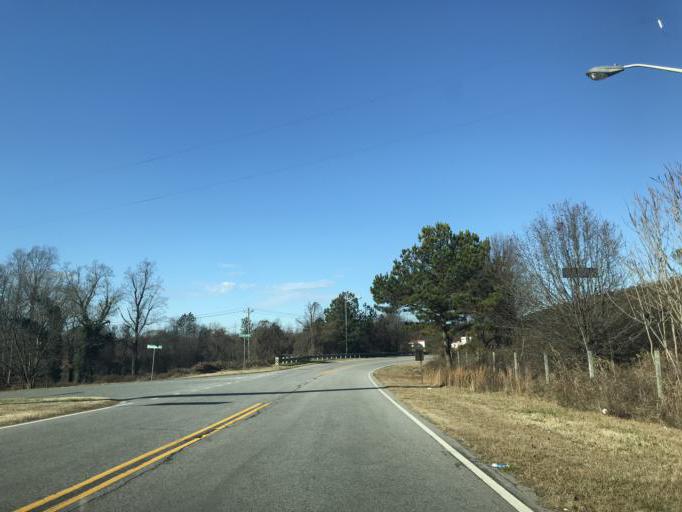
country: US
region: South Carolina
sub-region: Cherokee County
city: Gaffney
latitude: 35.0953
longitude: -81.6683
